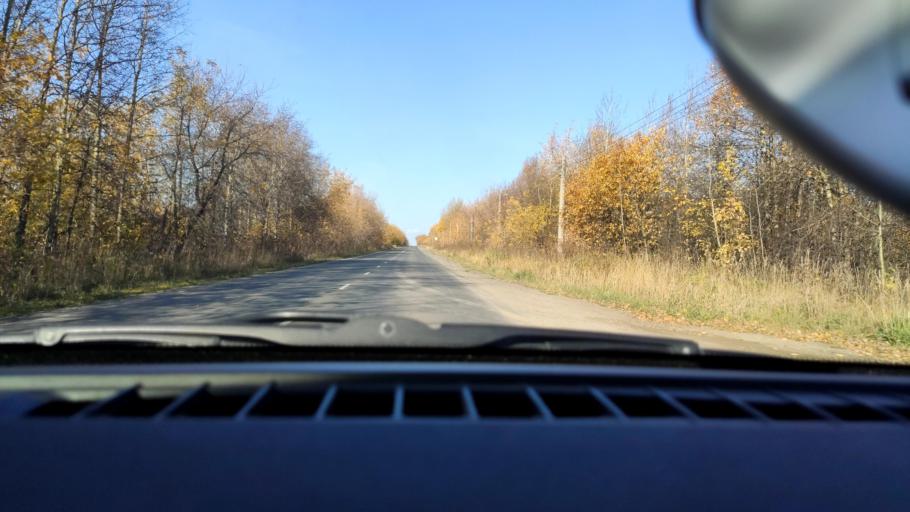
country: RU
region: Perm
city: Gamovo
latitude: 57.9006
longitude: 56.1772
